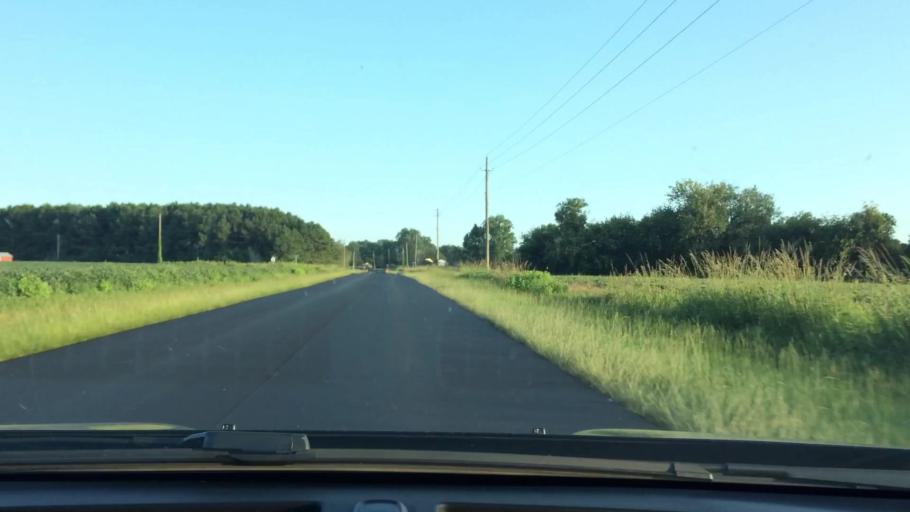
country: US
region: North Carolina
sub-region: Pitt County
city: Ayden
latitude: 35.4329
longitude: -77.4506
